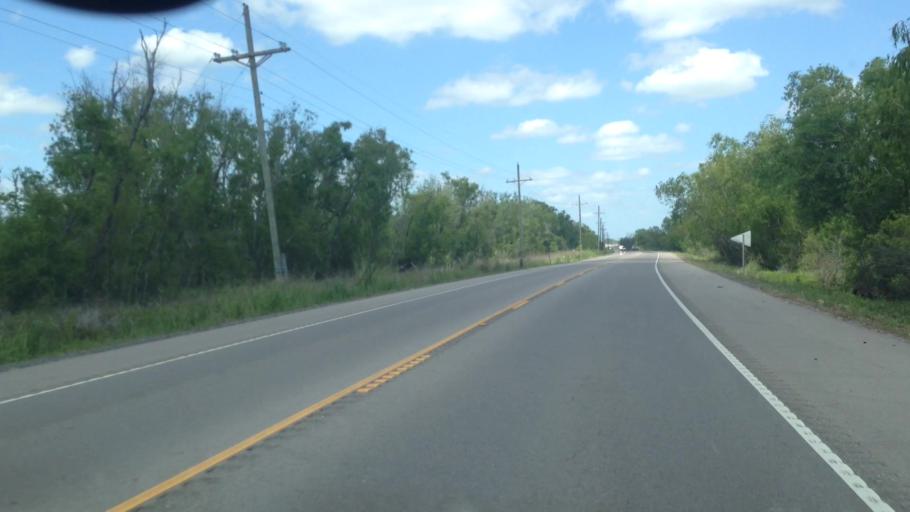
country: US
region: Louisiana
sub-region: Terrebonne Parish
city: Houma
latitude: 29.6357
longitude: -90.6995
